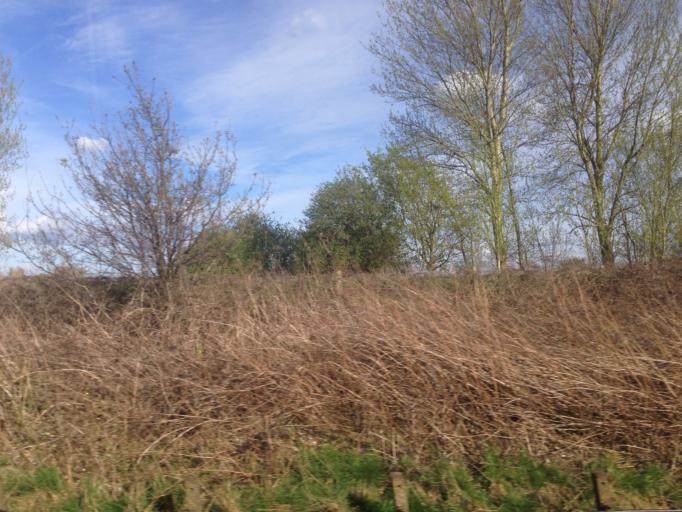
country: GB
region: England
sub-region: Greater London
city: Mitcham
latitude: 51.4010
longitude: -0.1585
